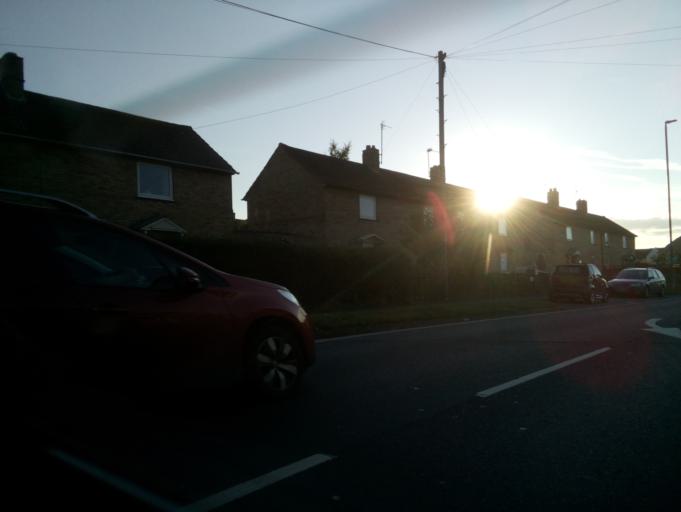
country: GB
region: England
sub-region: Gloucestershire
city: Tewkesbury
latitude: 51.9930
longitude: -2.1495
